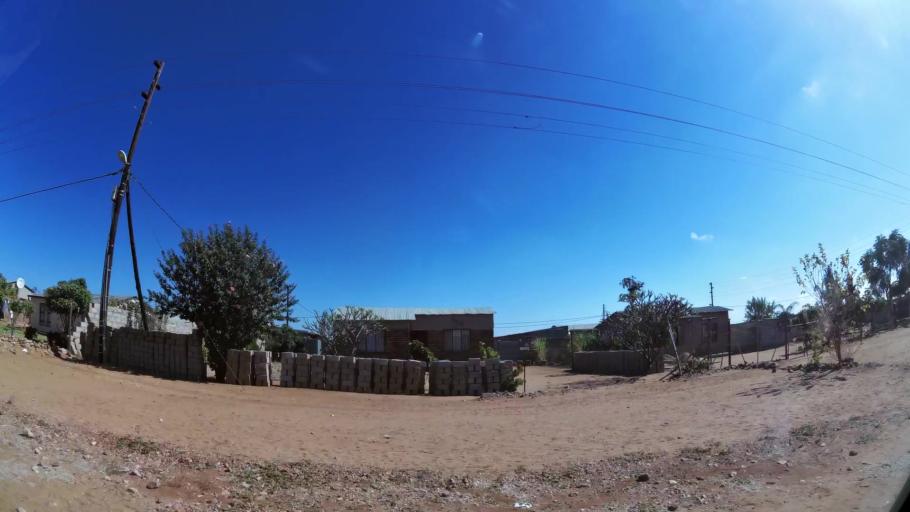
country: ZA
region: Limpopo
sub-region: Capricorn District Municipality
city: Polokwane
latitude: -23.8767
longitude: 29.4102
